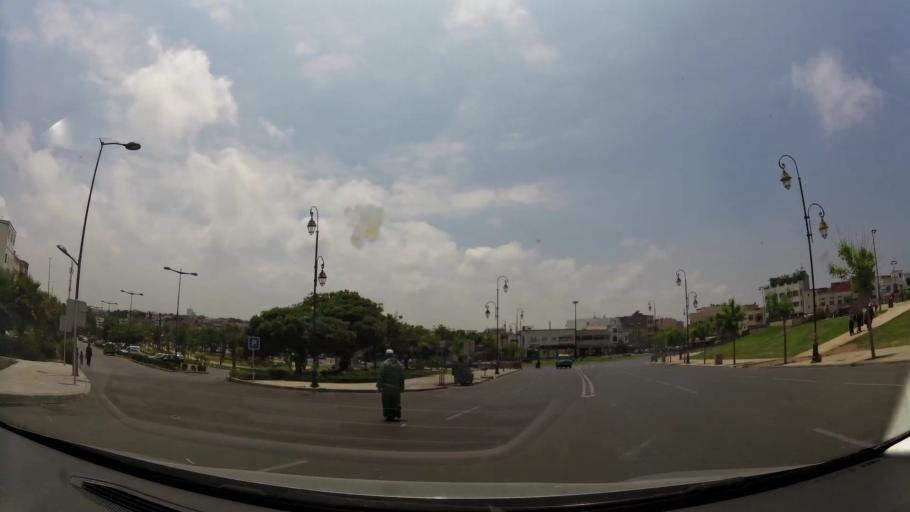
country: MA
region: Rabat-Sale-Zemmour-Zaer
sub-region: Skhirate-Temara
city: Temara
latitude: 33.9786
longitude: -6.8894
